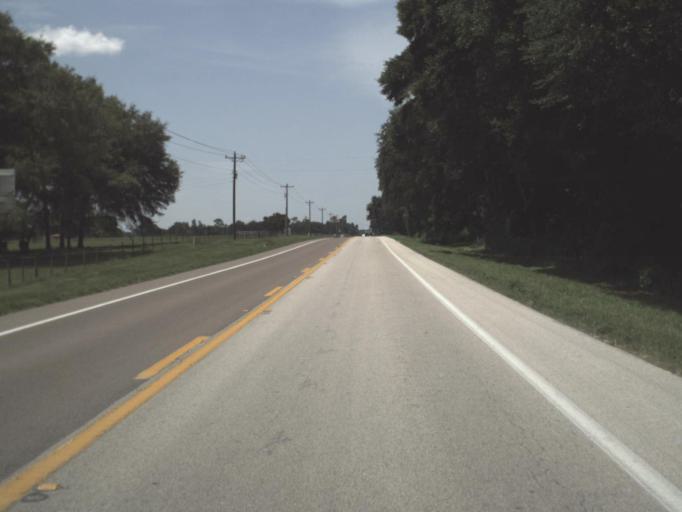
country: US
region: Florida
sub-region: Gilchrist County
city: Trenton
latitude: 29.7184
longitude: -82.8576
